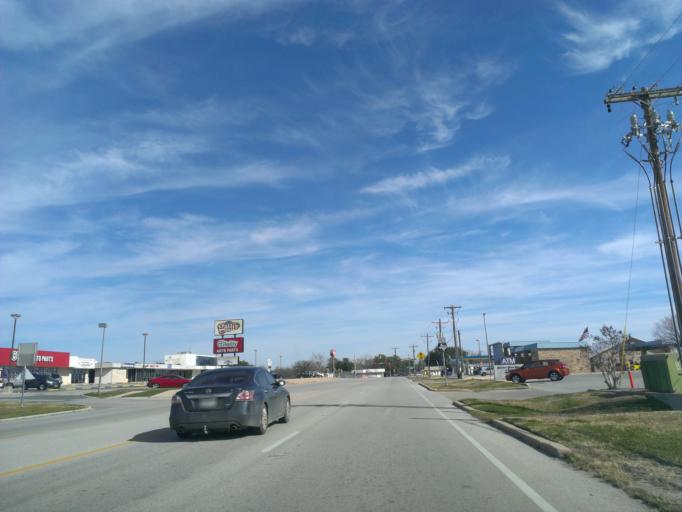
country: US
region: Texas
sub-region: Llano County
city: Kingsland
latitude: 30.6578
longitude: -98.4454
